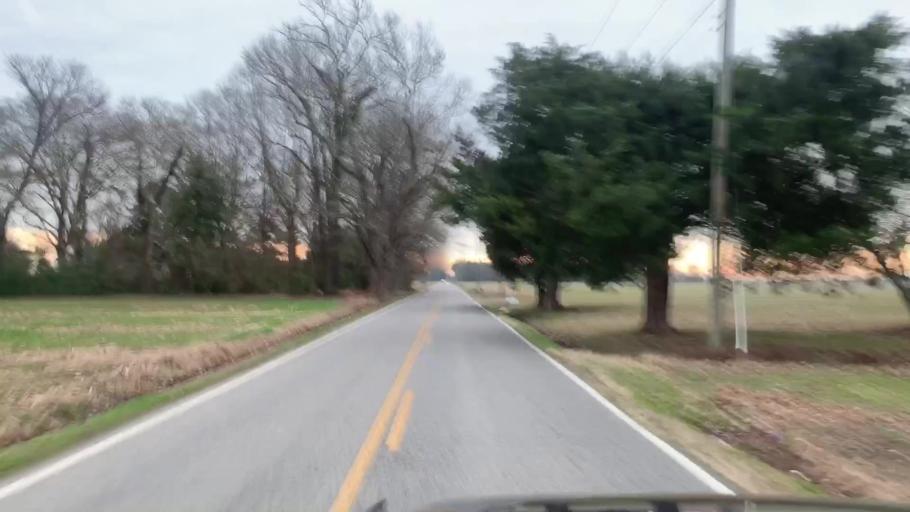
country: US
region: North Carolina
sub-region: Currituck County
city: Moyock
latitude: 36.6348
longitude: -76.1886
